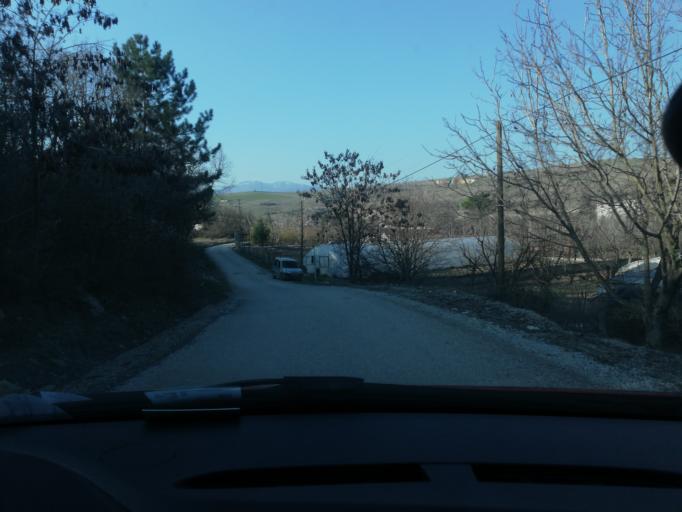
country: TR
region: Karabuk
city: Safranbolu
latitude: 41.2142
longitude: 32.7463
